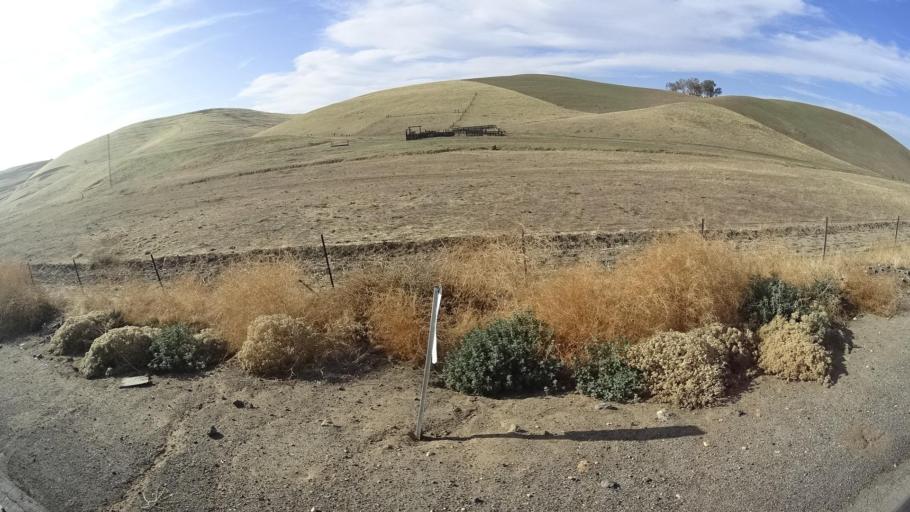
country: US
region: California
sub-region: Kern County
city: Oildale
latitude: 35.6152
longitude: -118.9833
